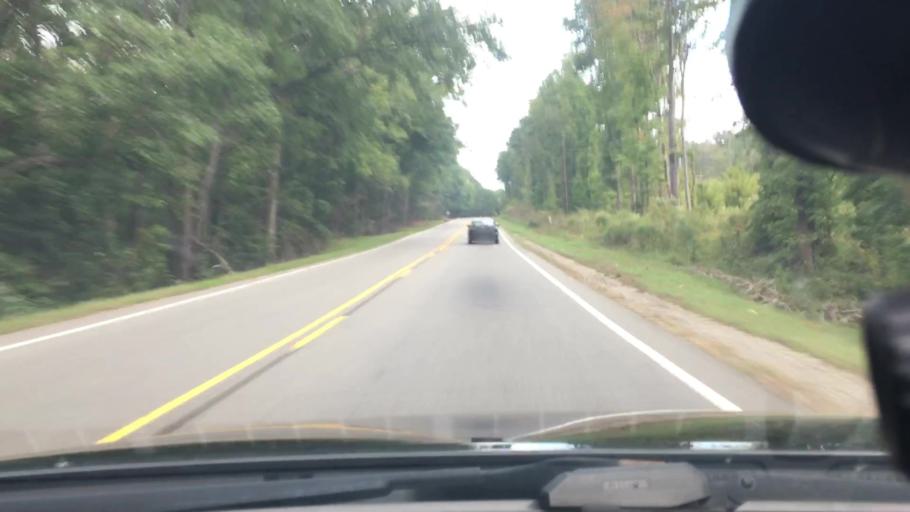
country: US
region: North Carolina
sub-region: Moore County
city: Carthage
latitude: 35.3610
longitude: -79.4390
